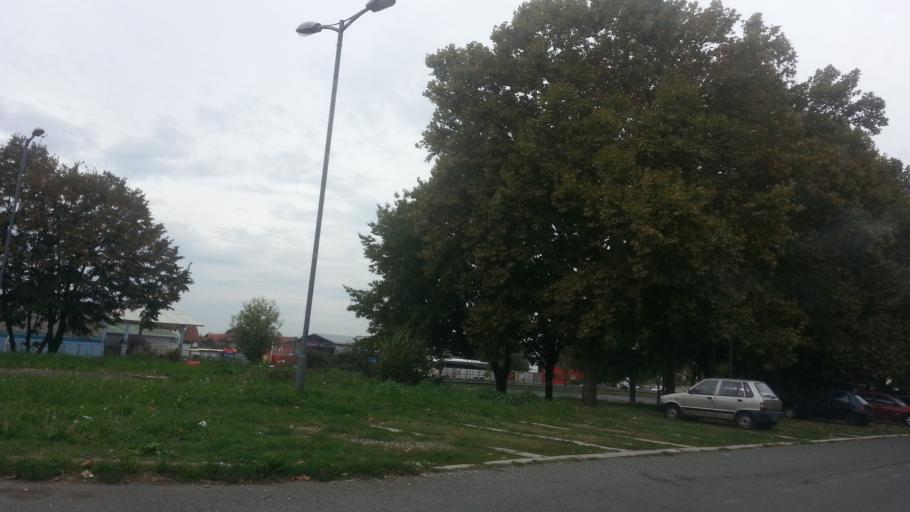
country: RS
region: Central Serbia
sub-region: Belgrade
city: Zemun
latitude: 44.8550
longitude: 20.3663
